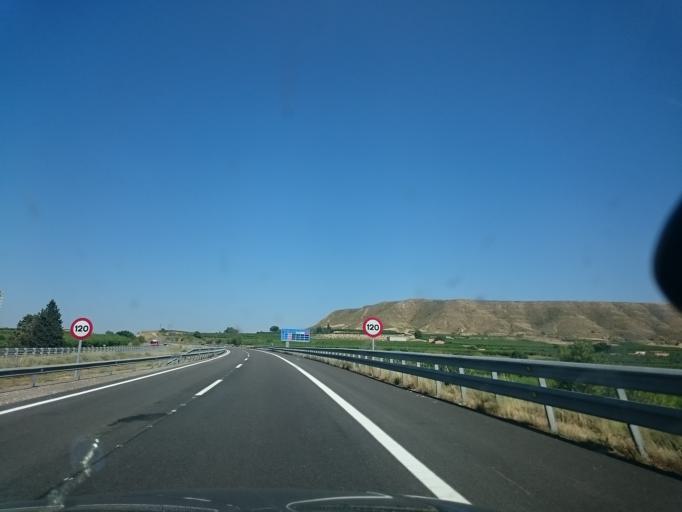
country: ES
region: Aragon
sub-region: Provincia de Huesca
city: Fraga
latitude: 41.4907
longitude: 0.3532
